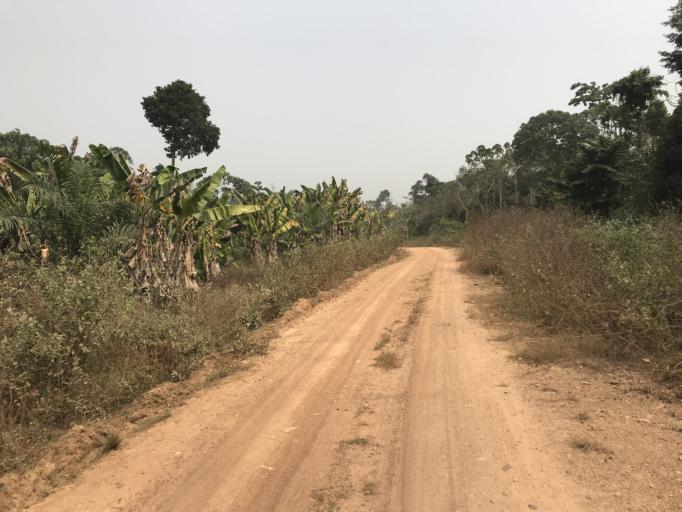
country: NG
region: Osun
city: Ifetedo
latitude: 7.0509
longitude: 4.4723
